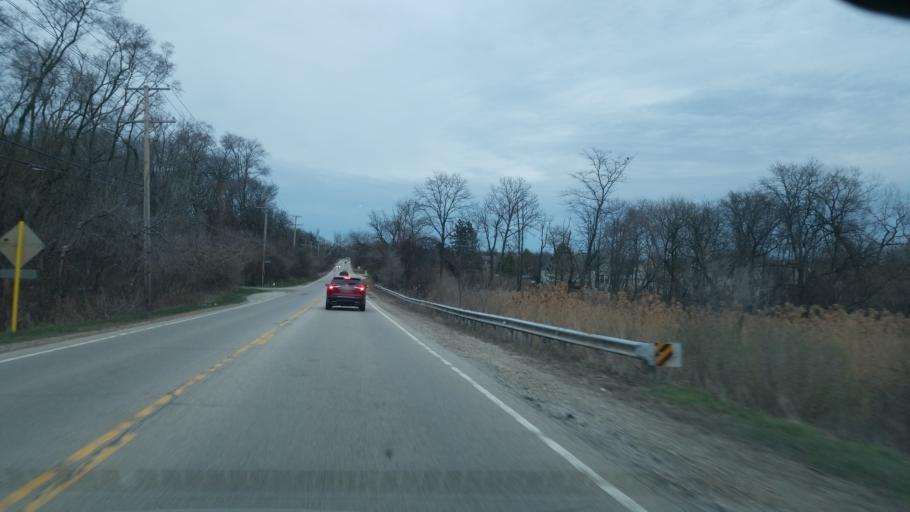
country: US
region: Illinois
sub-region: Kane County
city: Sleepy Hollow
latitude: 42.1032
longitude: -88.3264
